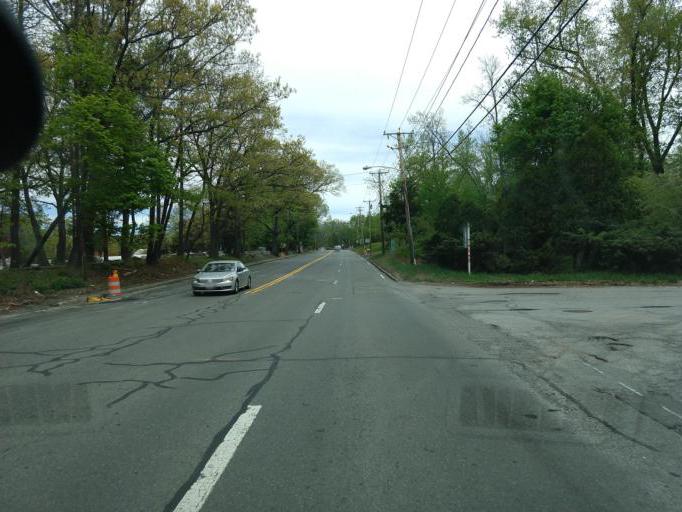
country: US
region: Massachusetts
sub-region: Essex County
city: North Andover
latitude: 42.7387
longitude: -71.1122
